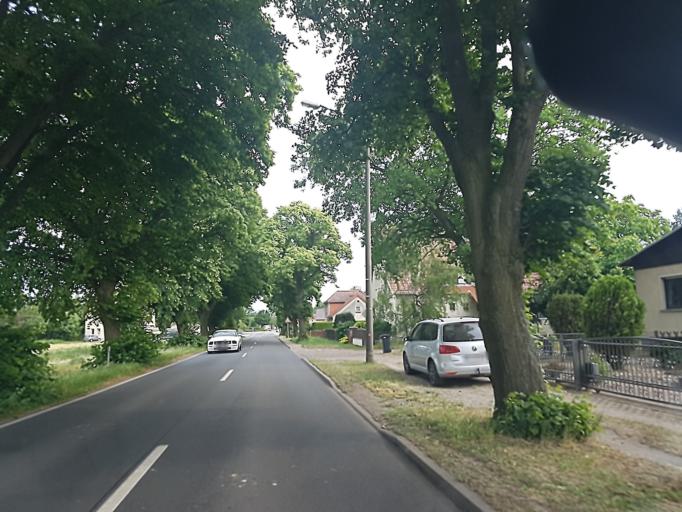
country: DE
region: Saxony-Anhalt
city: Wittenburg
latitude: 51.8802
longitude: 12.6306
